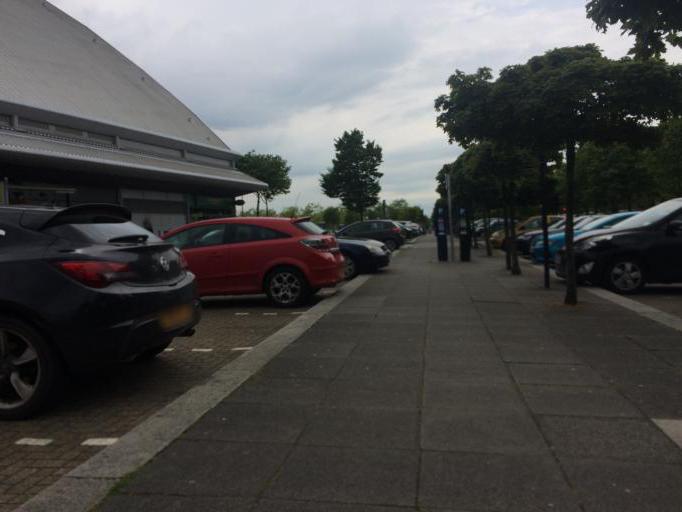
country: GB
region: England
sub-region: Milton Keynes
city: Milton Keynes
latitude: 52.0419
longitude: -0.7497
